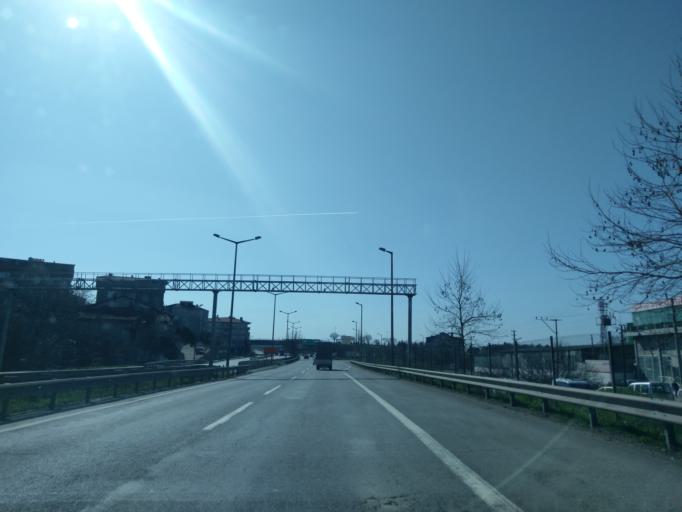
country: TR
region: Kocaeli
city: Darica
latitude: 40.8204
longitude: 29.3648
